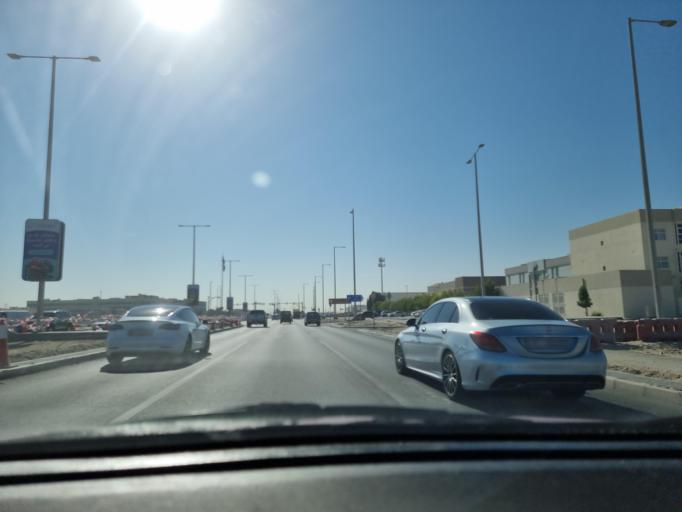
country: AE
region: Abu Dhabi
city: Abu Dhabi
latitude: 24.4160
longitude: 54.5679
